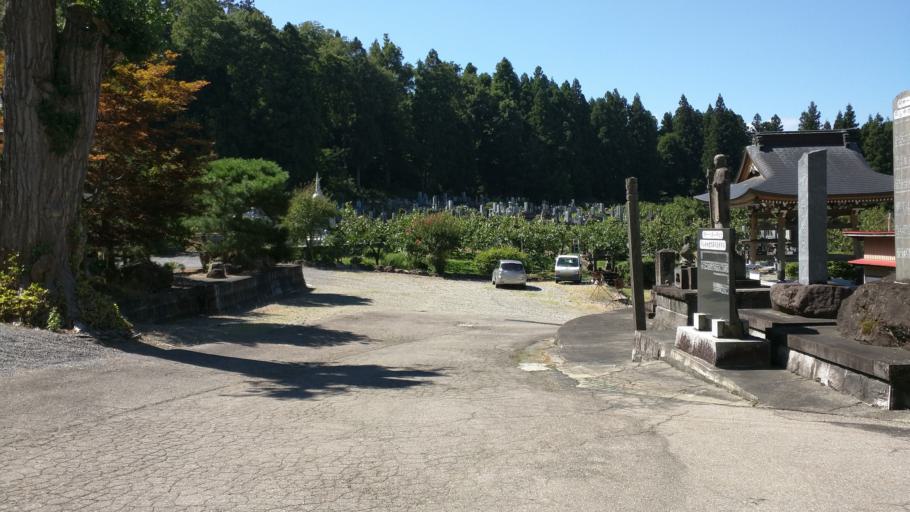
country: JP
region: Fukushima
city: Kitakata
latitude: 37.4556
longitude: 139.9374
